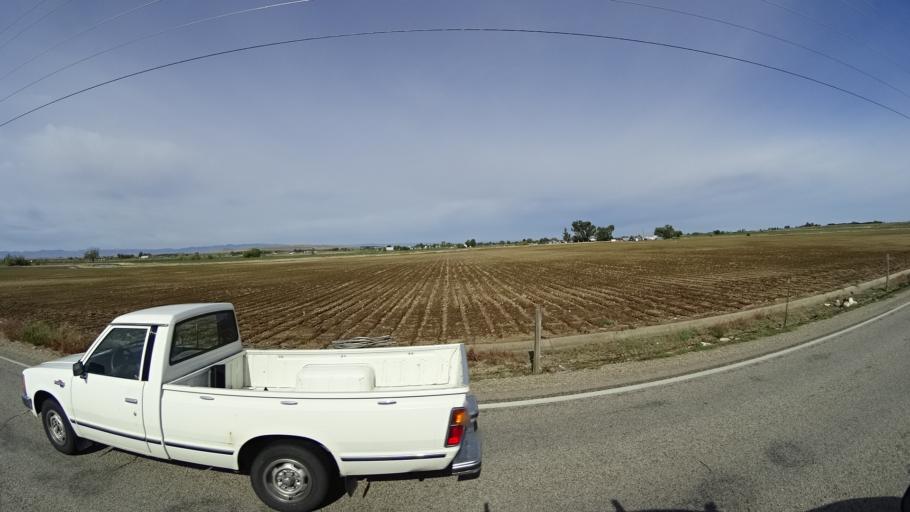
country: US
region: Idaho
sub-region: Ada County
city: Kuna
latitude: 43.4715
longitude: -116.3342
